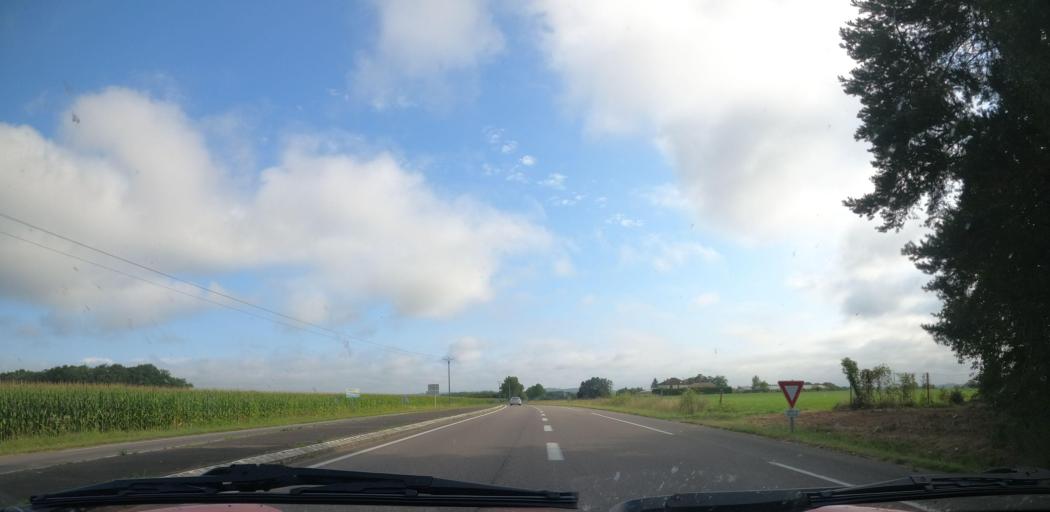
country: FR
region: Aquitaine
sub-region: Departement des Landes
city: Peyrehorade
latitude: 43.5199
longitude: -1.1063
